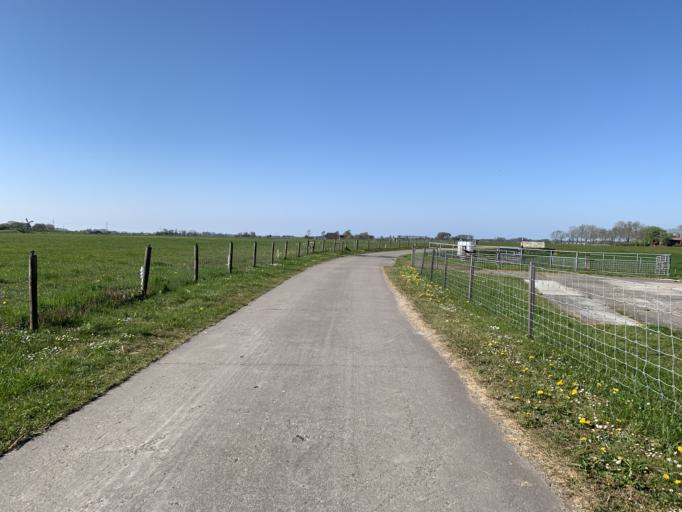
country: NL
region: Groningen
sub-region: Gemeente Winsum
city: Winsum
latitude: 53.2962
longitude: 6.5059
